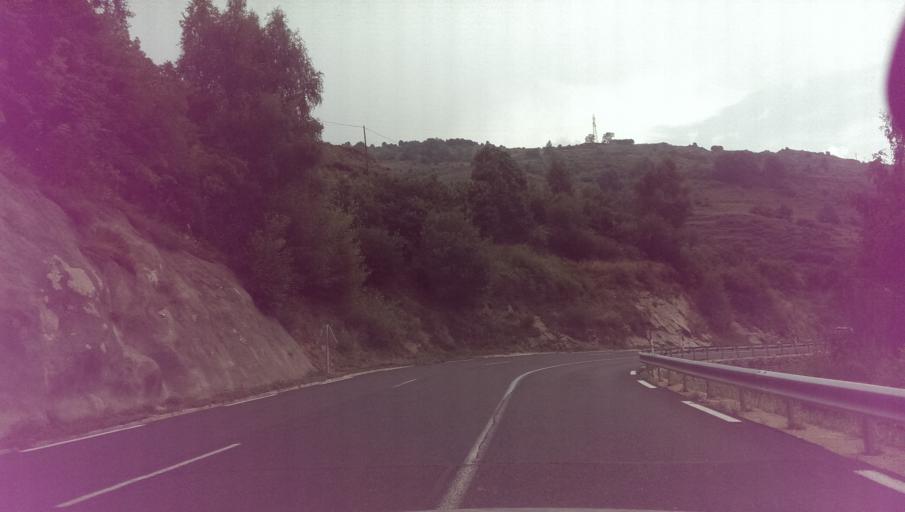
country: ES
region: Catalonia
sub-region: Provincia de Girona
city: Llivia
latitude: 42.5073
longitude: 2.1361
